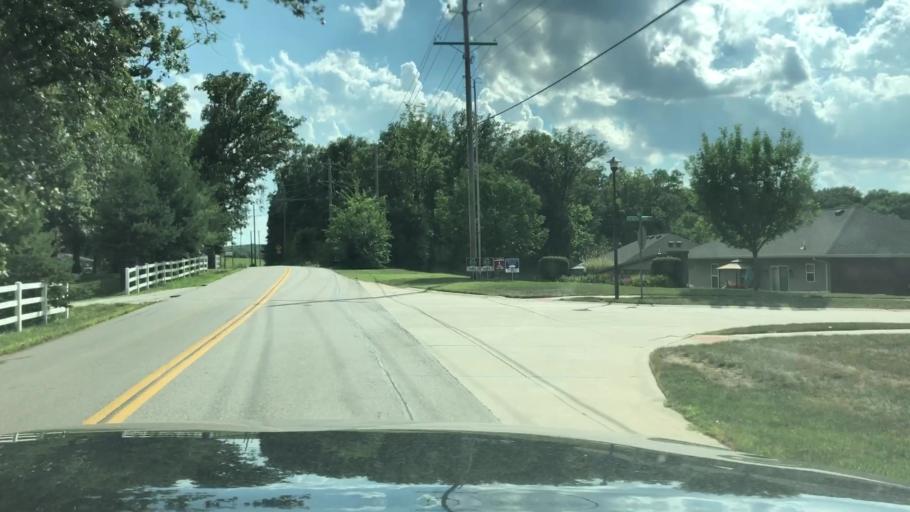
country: US
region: Missouri
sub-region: Saint Charles County
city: Wentzville
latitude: 38.8488
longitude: -90.8817
